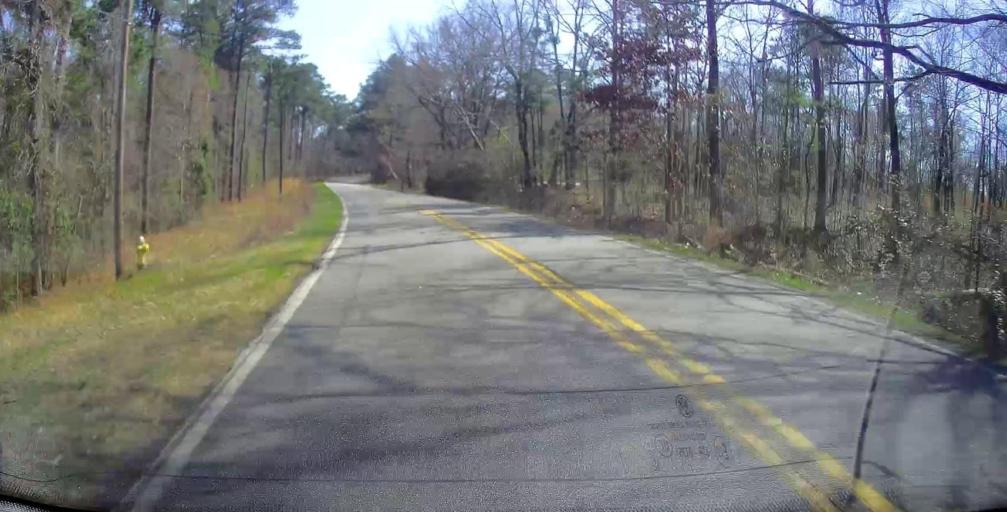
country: US
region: Georgia
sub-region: Bibb County
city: Macon
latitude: 32.8832
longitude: -83.6311
